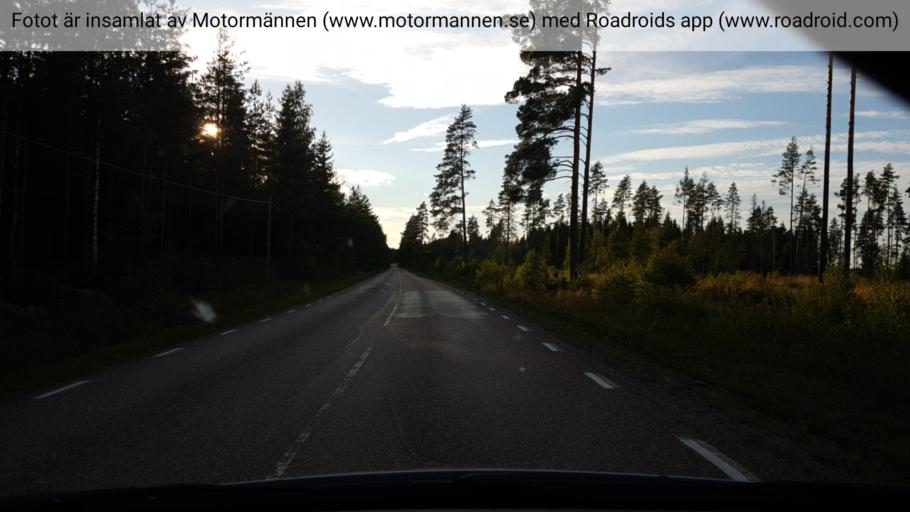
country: SE
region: Vaestmanland
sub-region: Surahammars Kommun
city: Surahammar
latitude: 59.7539
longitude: 16.3171
